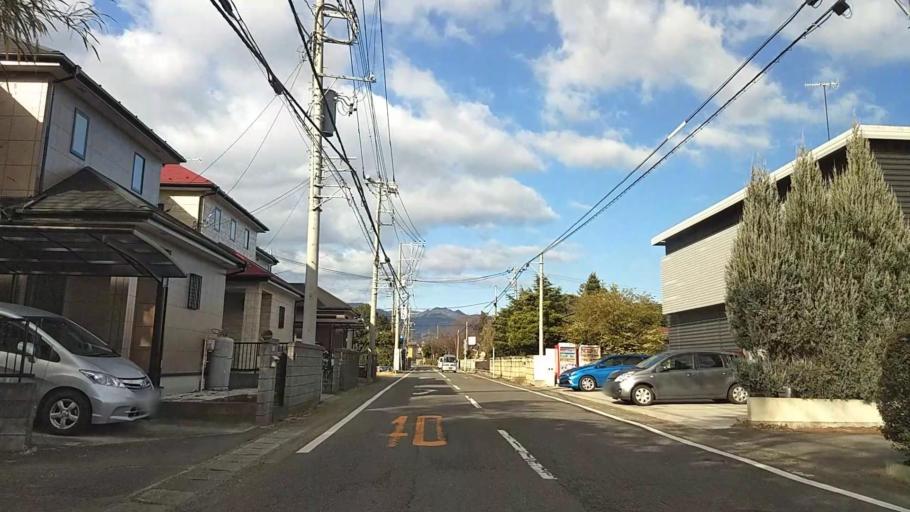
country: JP
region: Kanagawa
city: Atsugi
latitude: 35.4165
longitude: 139.3580
